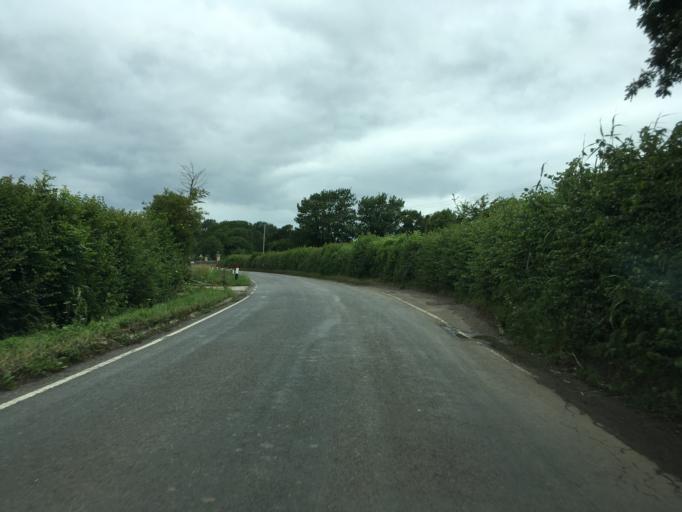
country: GB
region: England
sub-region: Gloucestershire
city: Stonehouse
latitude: 51.7781
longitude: -2.3781
